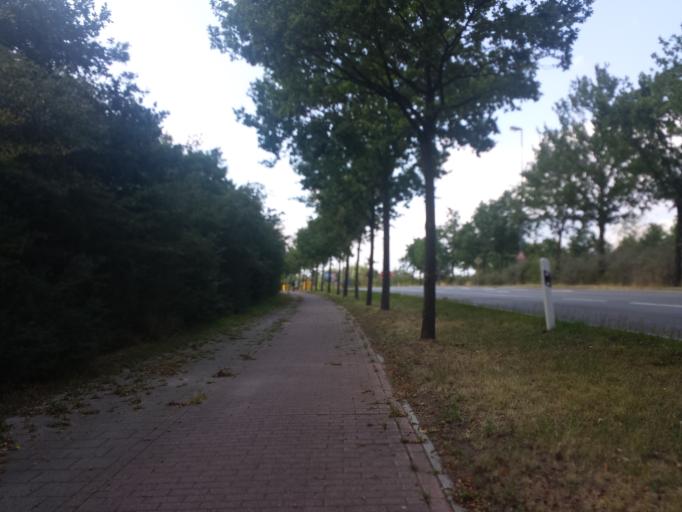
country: DE
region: Lower Saxony
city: Stuhr
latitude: 53.0850
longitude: 8.7309
